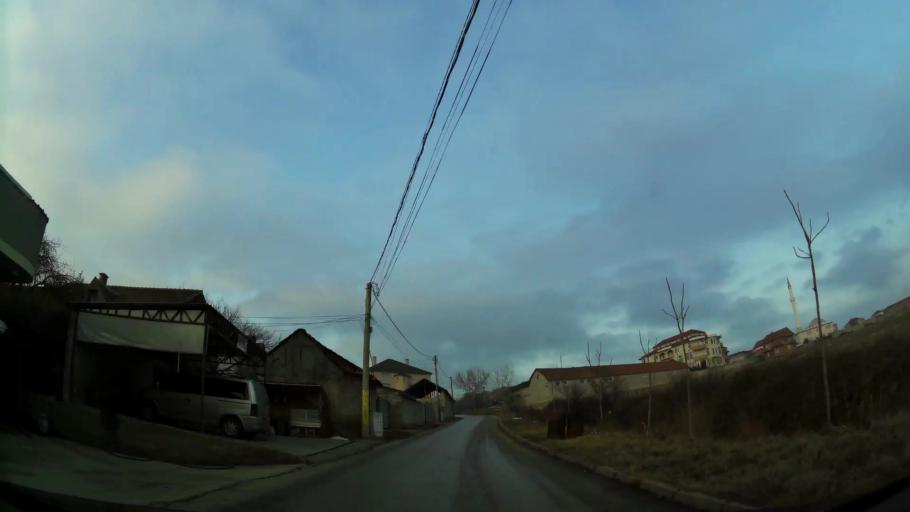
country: MK
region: Aracinovo
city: Arachinovo
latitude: 42.0266
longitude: 21.5734
